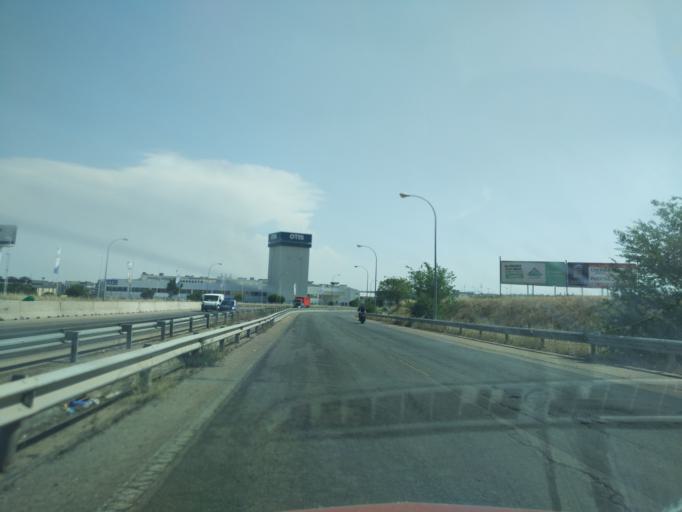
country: ES
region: Madrid
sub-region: Provincia de Madrid
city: Latina
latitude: 40.3583
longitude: -3.7476
